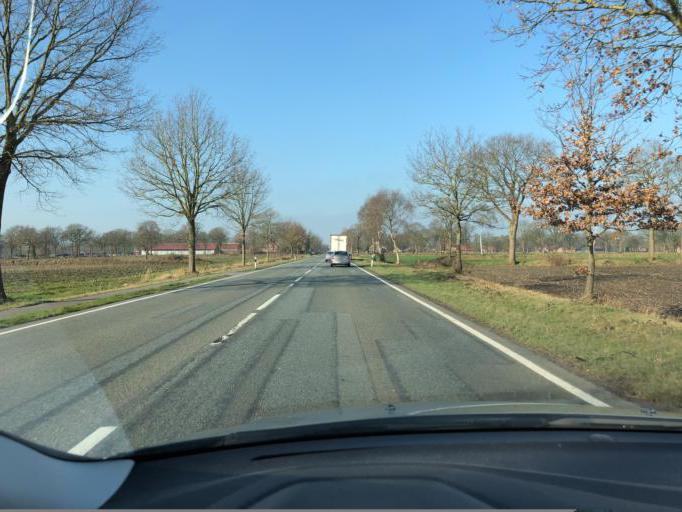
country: DE
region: Lower Saxony
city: Apen
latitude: 53.3011
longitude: 7.7937
